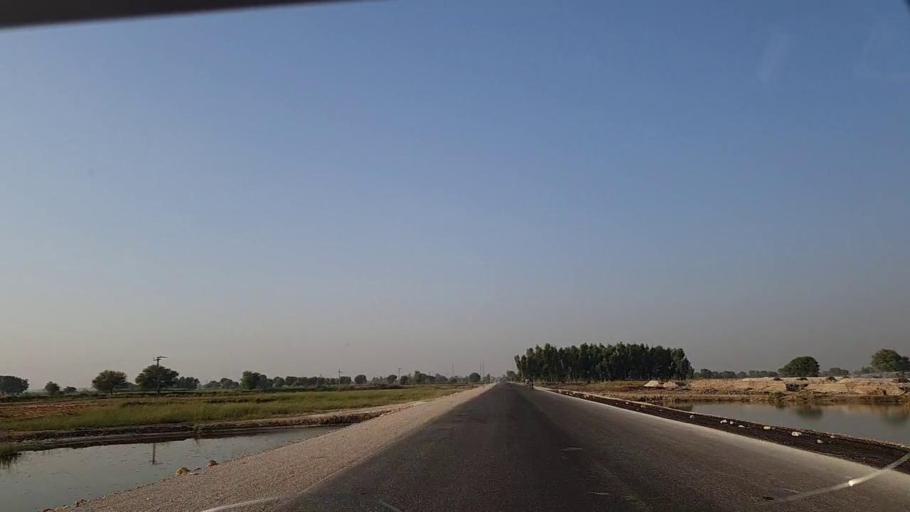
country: PK
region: Sindh
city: Rustam jo Goth
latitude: 27.9495
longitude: 68.8095
